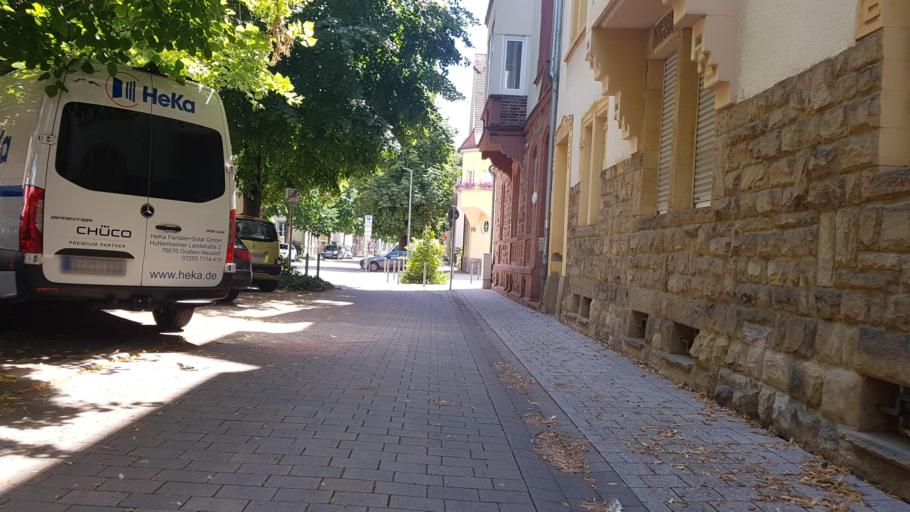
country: DE
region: Baden-Wuerttemberg
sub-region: Karlsruhe Region
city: Bruchsal
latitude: 49.1285
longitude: 8.5945
